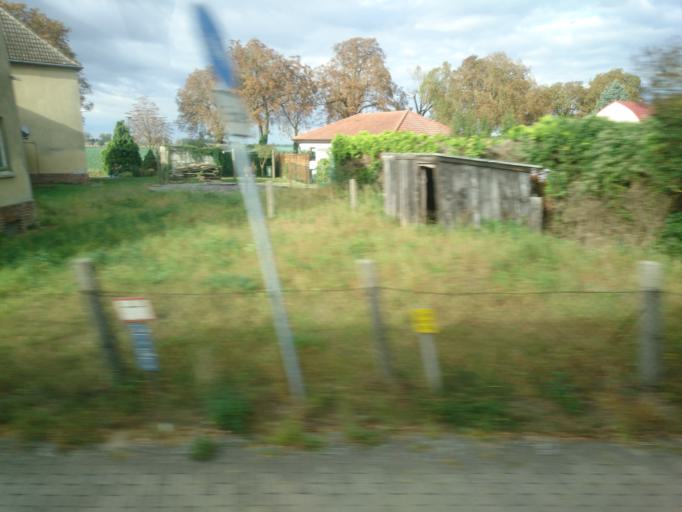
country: DE
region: Mecklenburg-Vorpommern
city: Pasewalk
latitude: 53.5181
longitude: 13.9776
